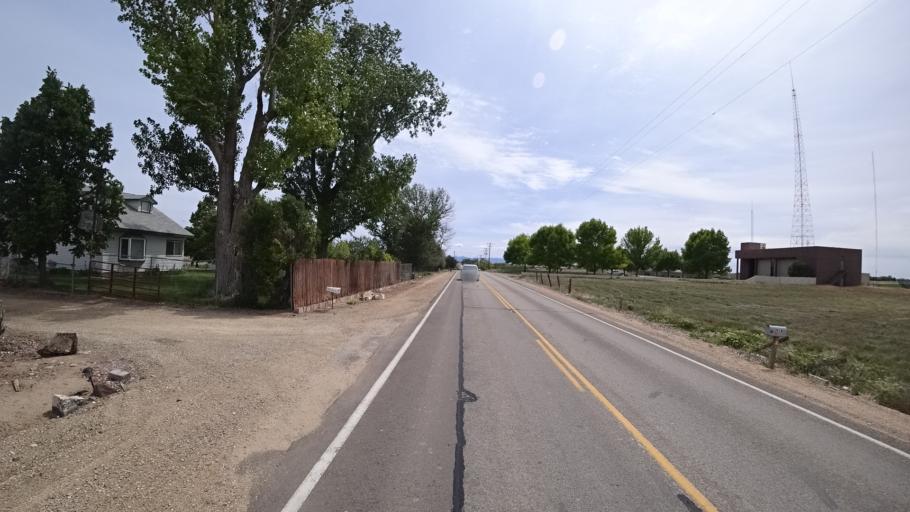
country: US
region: Idaho
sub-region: Ada County
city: Meridian
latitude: 43.5611
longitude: -116.4004
